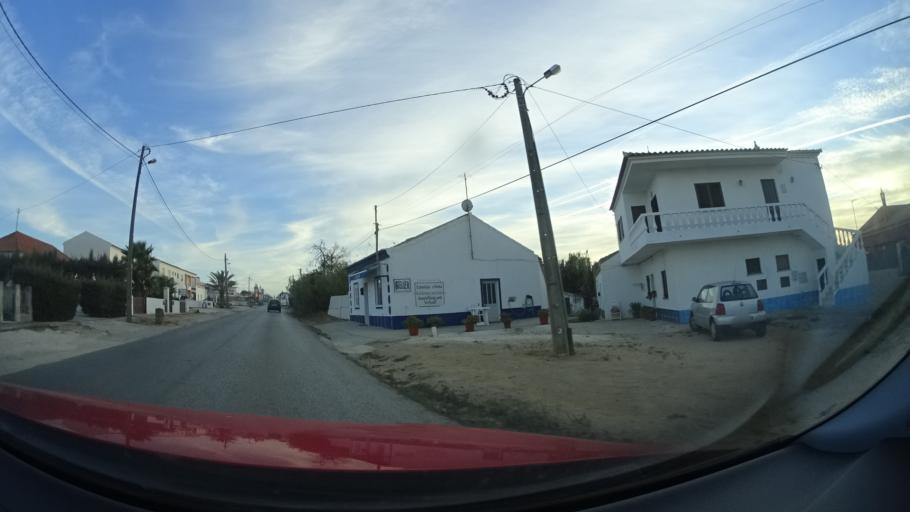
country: PT
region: Faro
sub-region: Vila do Bispo
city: Sagres
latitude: 37.0168
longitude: -8.9410
